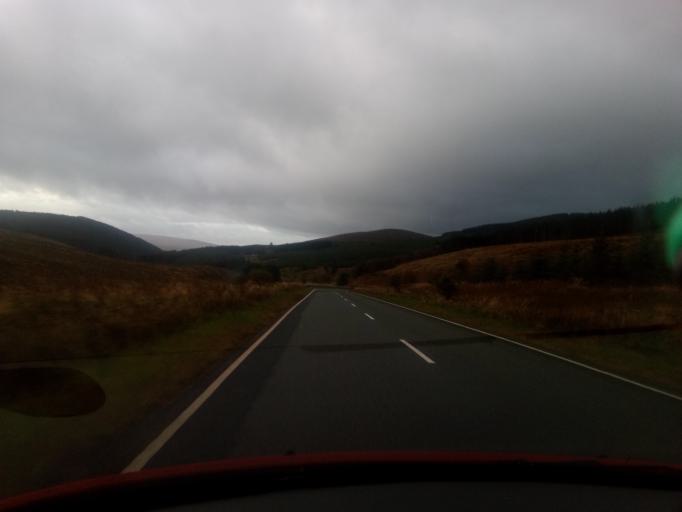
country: GB
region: Scotland
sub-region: The Scottish Borders
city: Hawick
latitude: 55.3163
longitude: -2.6518
